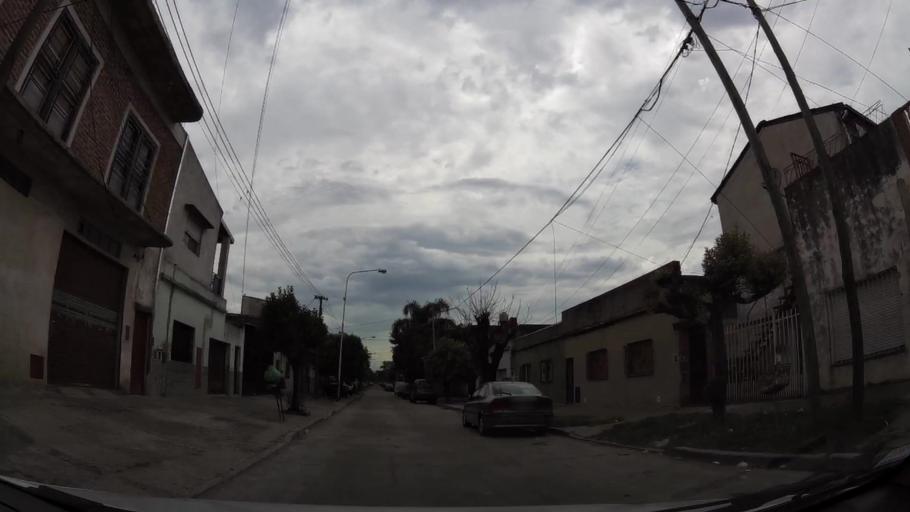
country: AR
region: Buenos Aires F.D.
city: Villa Lugano
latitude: -34.6799
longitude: -58.5045
